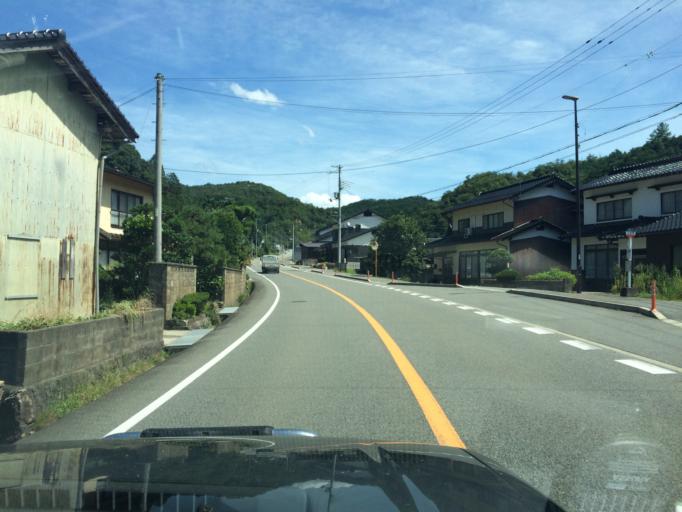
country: JP
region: Hyogo
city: Toyooka
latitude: 35.4401
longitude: 134.8066
